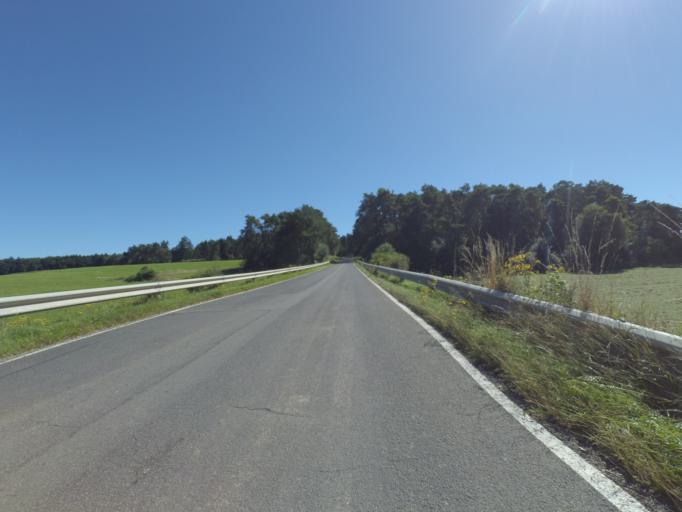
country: DE
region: Rheinland-Pfalz
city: Uxheim
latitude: 50.3271
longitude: 6.7553
